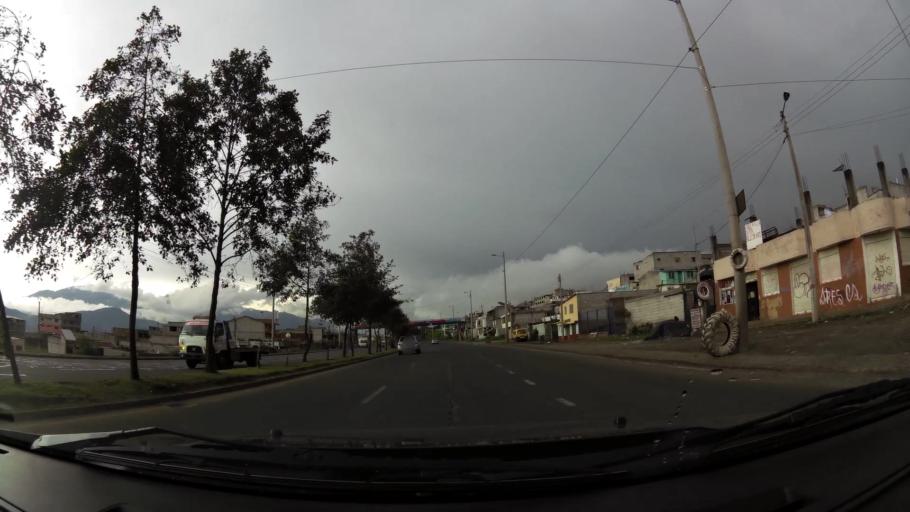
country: EC
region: Pichincha
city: Quito
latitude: -0.2996
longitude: -78.5209
